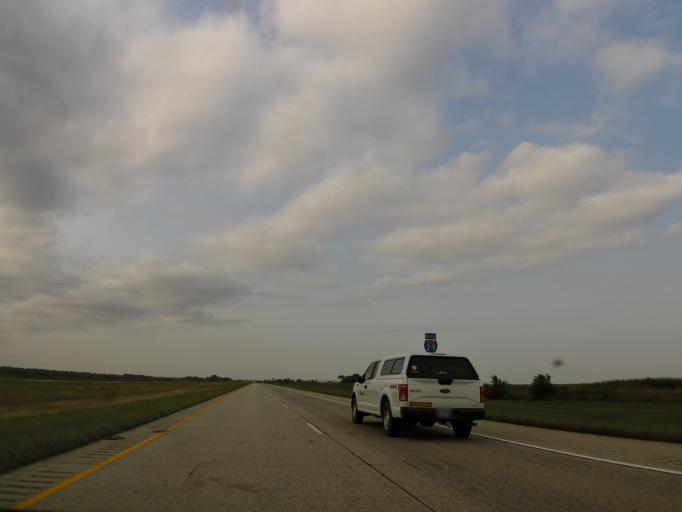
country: US
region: North Dakota
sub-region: Richland County
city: Wahpeton
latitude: 46.3906
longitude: -96.8301
